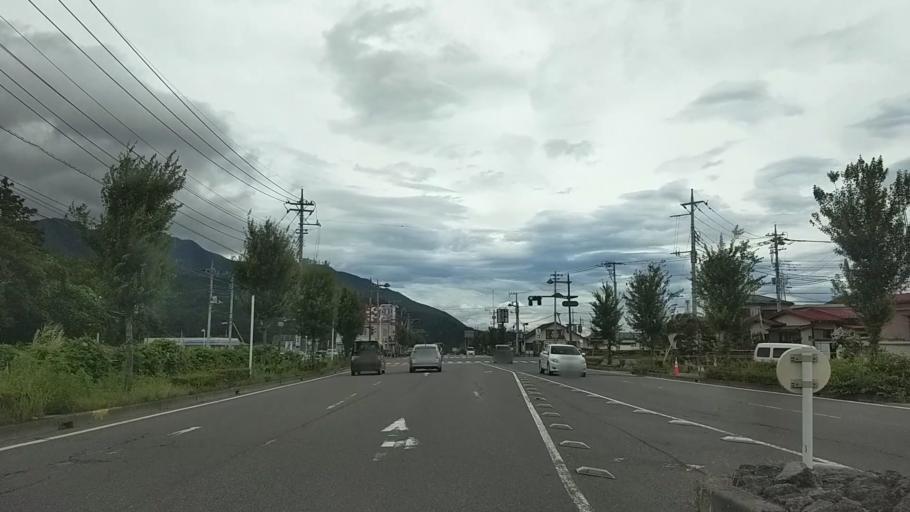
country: JP
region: Yamanashi
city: Fujikawaguchiko
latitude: 35.4903
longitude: 138.8136
